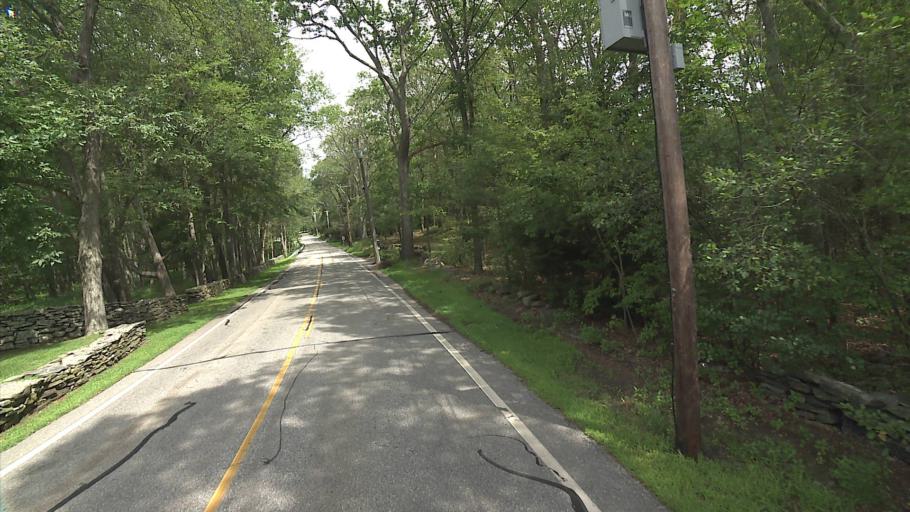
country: US
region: Connecticut
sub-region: Windham County
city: Thompson
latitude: 41.9470
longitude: -71.8644
